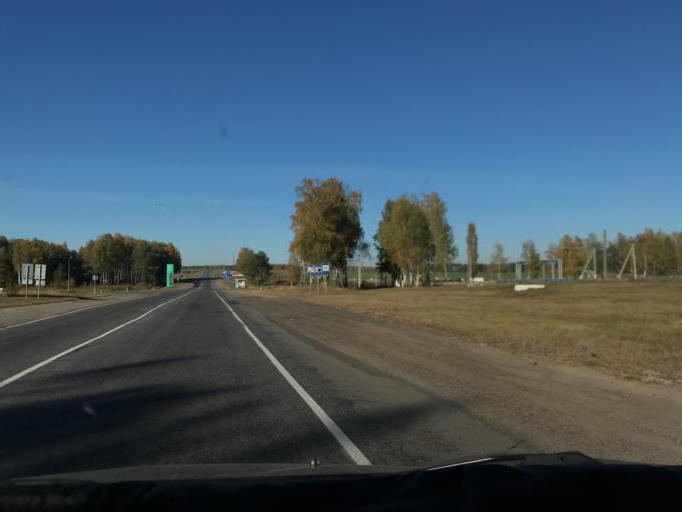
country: BY
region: Gomel
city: Mazyr
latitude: 51.9979
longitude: 29.2578
